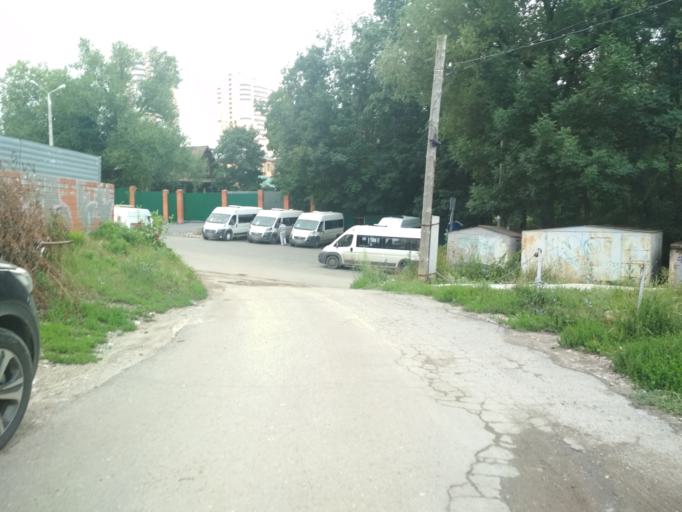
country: RU
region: Tula
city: Mendeleyevskiy
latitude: 54.1541
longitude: 37.5782
